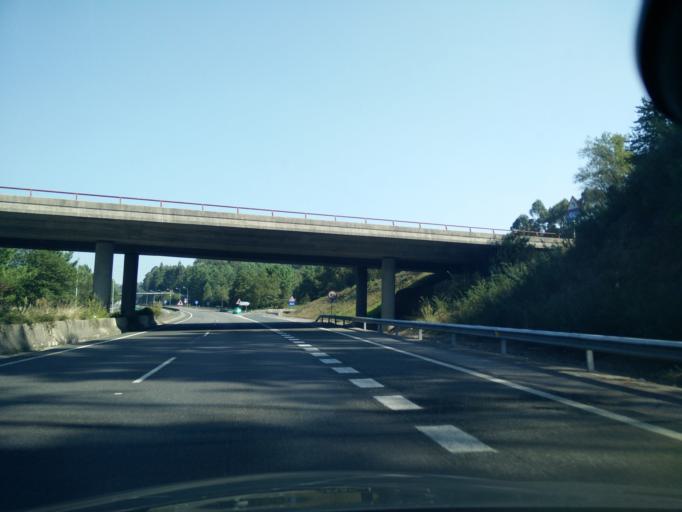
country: ES
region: Galicia
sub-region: Provincia da Coruna
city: Mino
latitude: 43.3740
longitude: -8.1858
